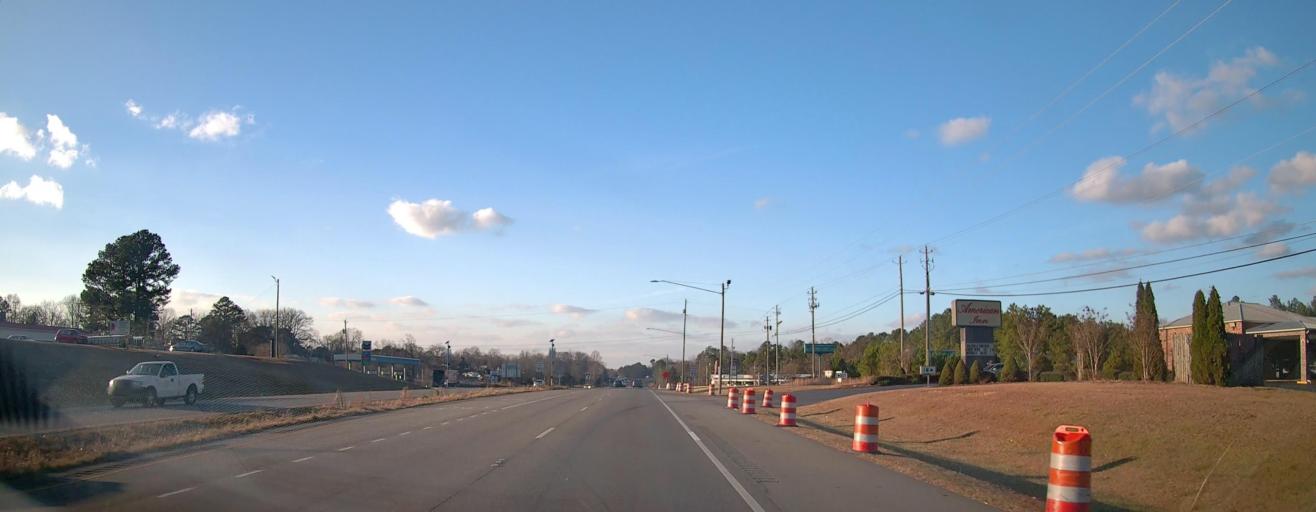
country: US
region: Alabama
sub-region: Calhoun County
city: Saks
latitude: 33.7034
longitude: -85.8317
